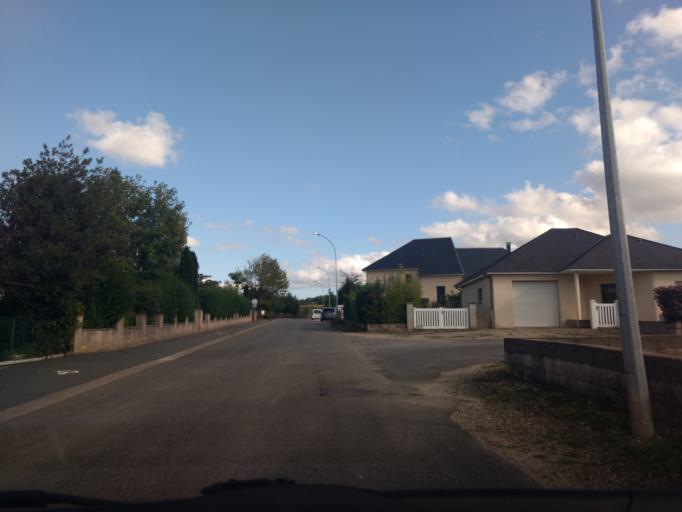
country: FR
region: Midi-Pyrenees
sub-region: Departement de l'Aveyron
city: Colombies
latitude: 44.4046
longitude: 2.2963
